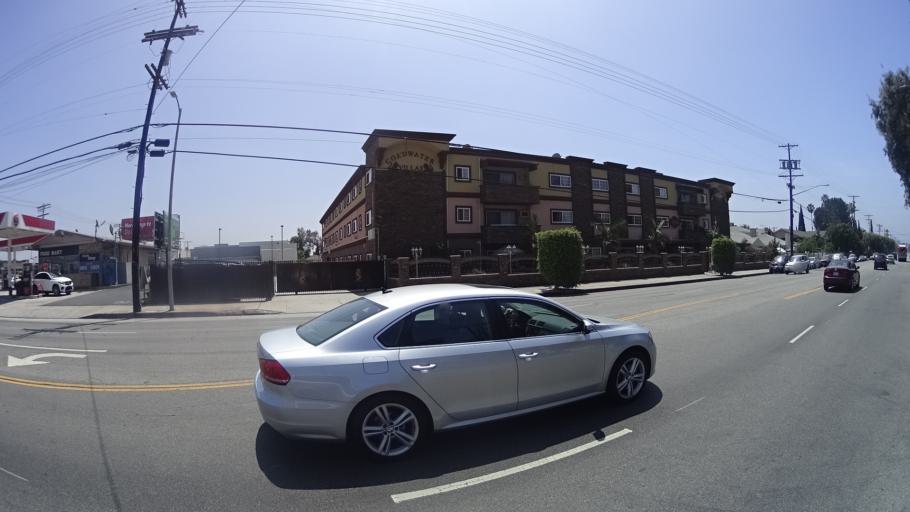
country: US
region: California
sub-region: Los Angeles County
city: Van Nuys
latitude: 34.2008
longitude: -118.4139
